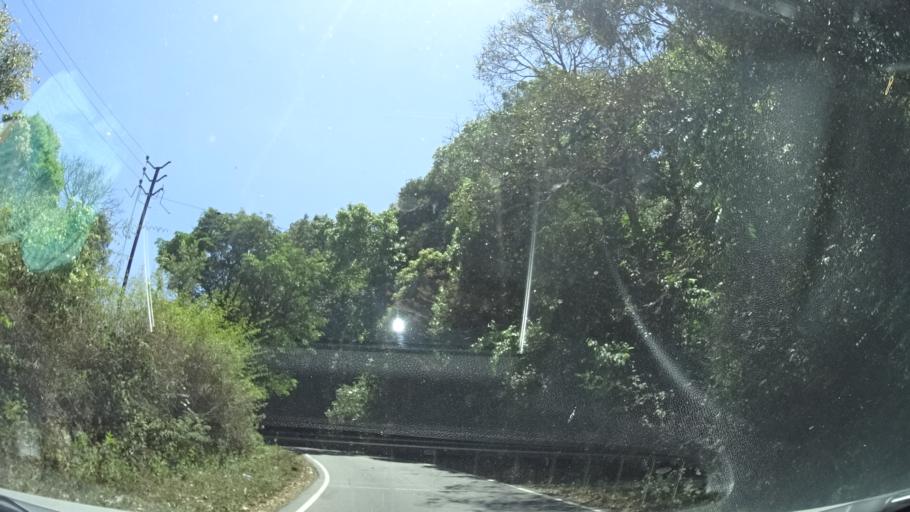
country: IN
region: Karnataka
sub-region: Chikmagalur
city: Sringeri
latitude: 13.1963
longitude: 75.2895
